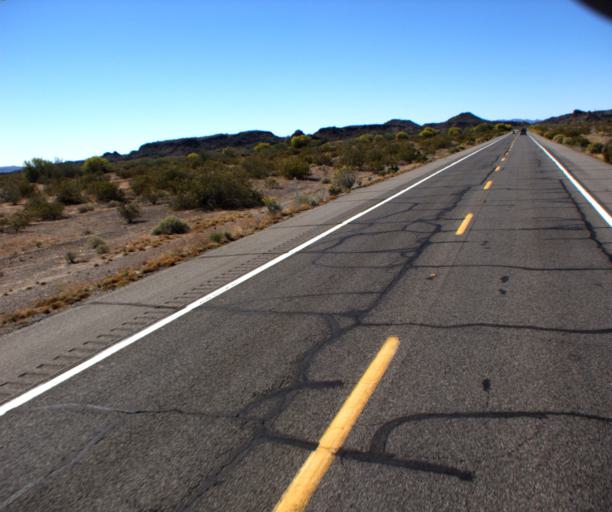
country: US
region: Arizona
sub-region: Pima County
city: Ajo
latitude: 32.5768
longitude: -112.8745
